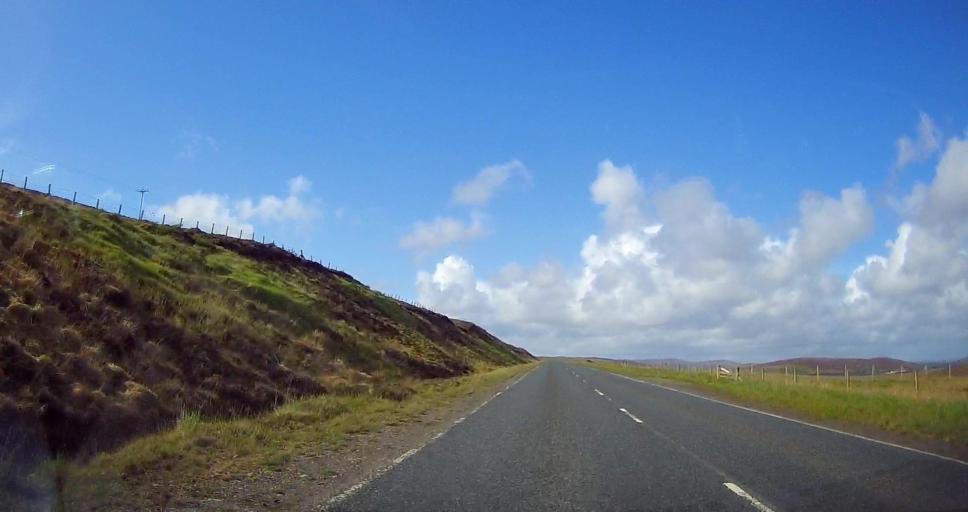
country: GB
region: Scotland
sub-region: Shetland Islands
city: Lerwick
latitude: 60.2165
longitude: -1.2339
